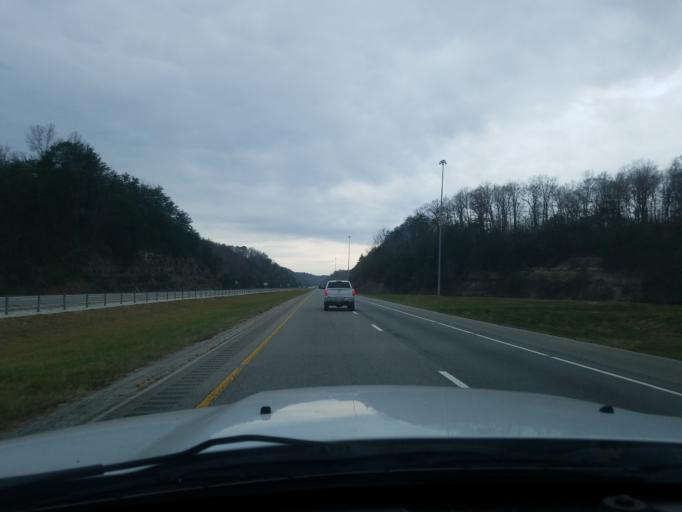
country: US
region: Kentucky
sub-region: Boyd County
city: Meads
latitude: 38.3657
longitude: -82.7738
